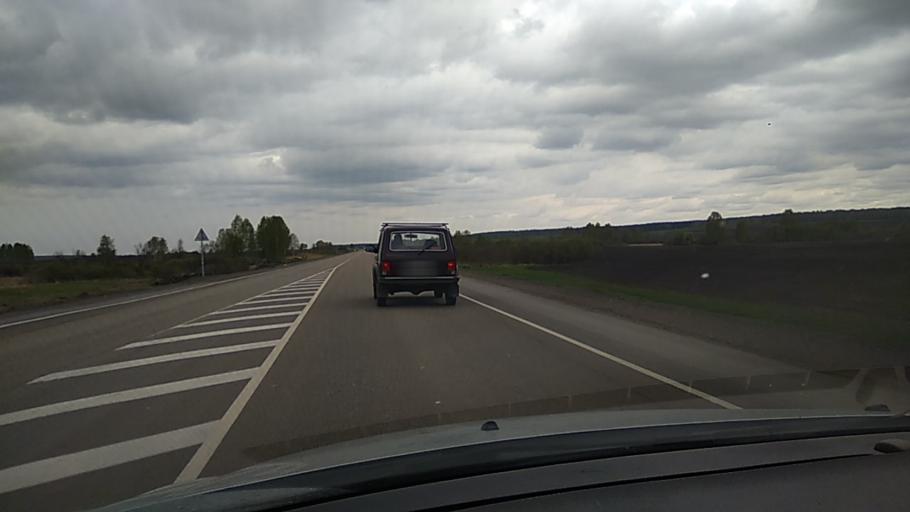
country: RU
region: Kurgan
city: Kataysk
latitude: 56.2980
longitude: 62.4472
